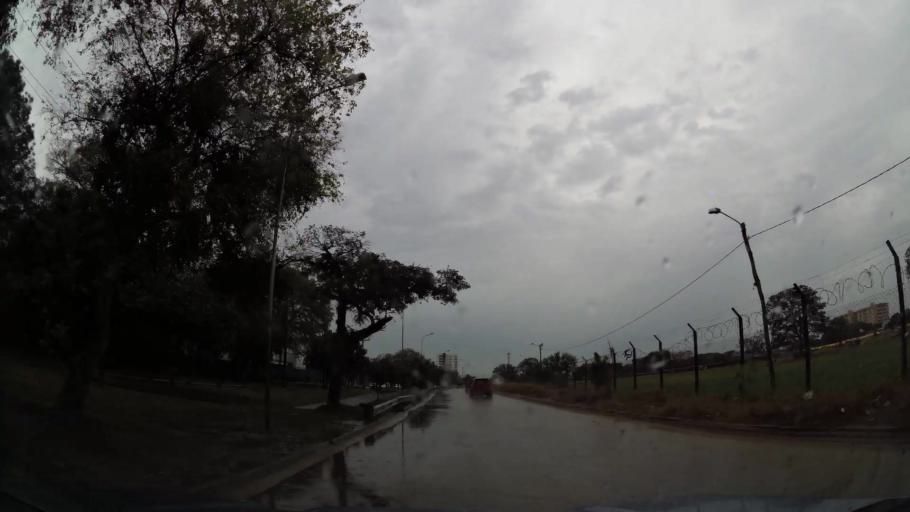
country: BO
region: Santa Cruz
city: Santa Cruz de la Sierra
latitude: -17.8015
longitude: -63.2255
